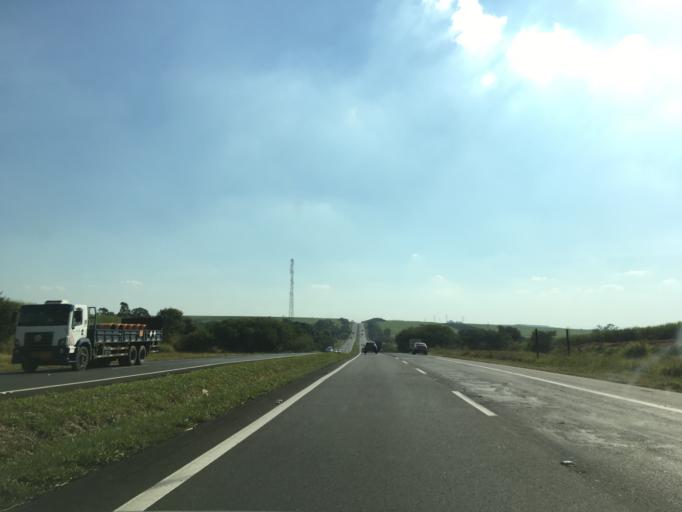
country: BR
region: Sao Paulo
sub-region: Piracicaba
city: Piracicaba
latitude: -22.7271
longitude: -47.5533
